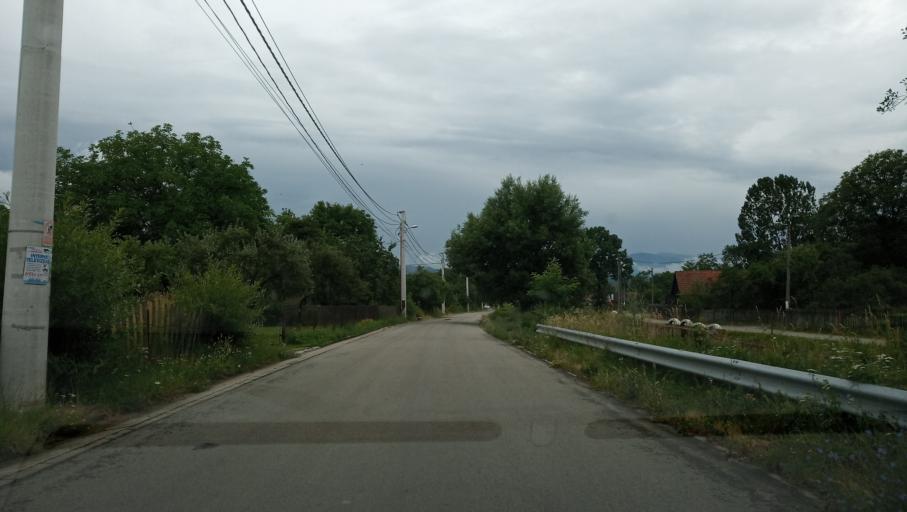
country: RO
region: Hunedoara
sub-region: Oras Petrila
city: Petrila
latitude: 45.4598
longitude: 23.4193
